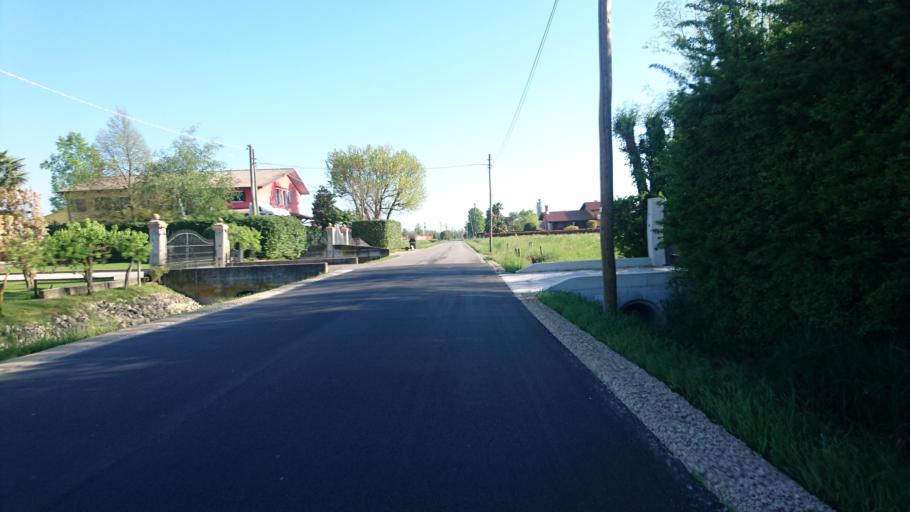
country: IT
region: Veneto
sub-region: Provincia di Venezia
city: Sant'Angelo
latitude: 45.5312
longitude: 12.0023
